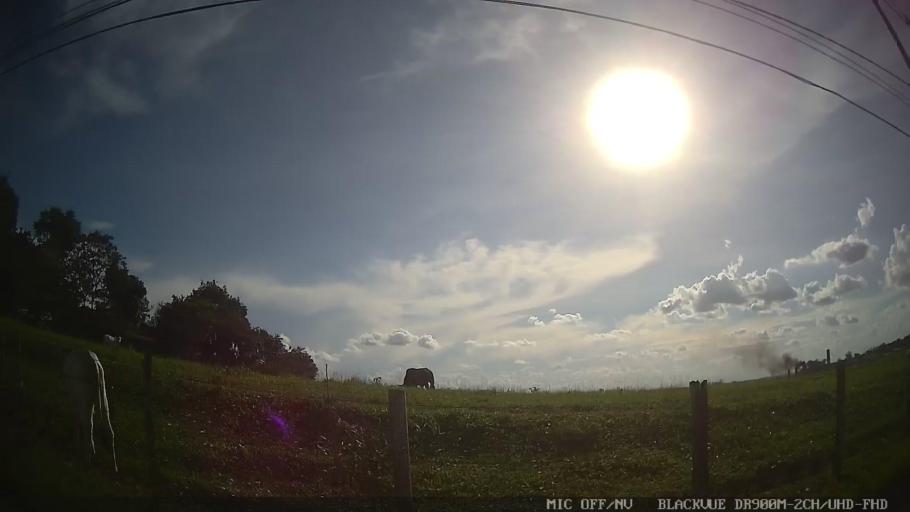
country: BR
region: Sao Paulo
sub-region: Tiete
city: Tiete
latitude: -23.0955
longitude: -47.7773
